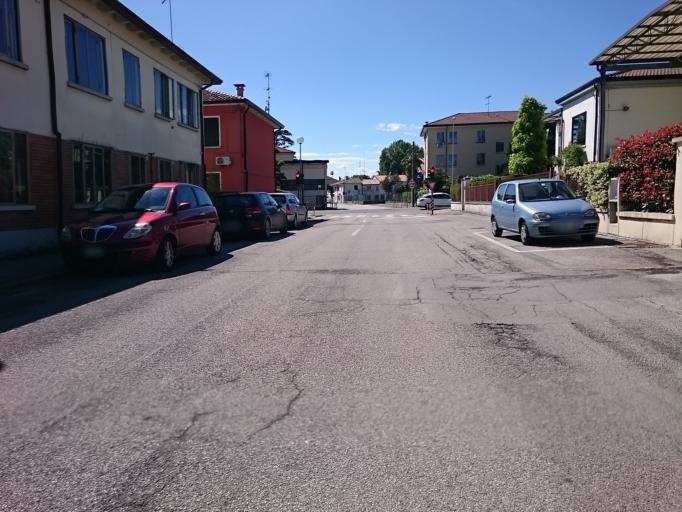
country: IT
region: Veneto
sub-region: Provincia di Padova
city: Piove di Sacco-Piovega
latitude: 45.2936
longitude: 12.0382
